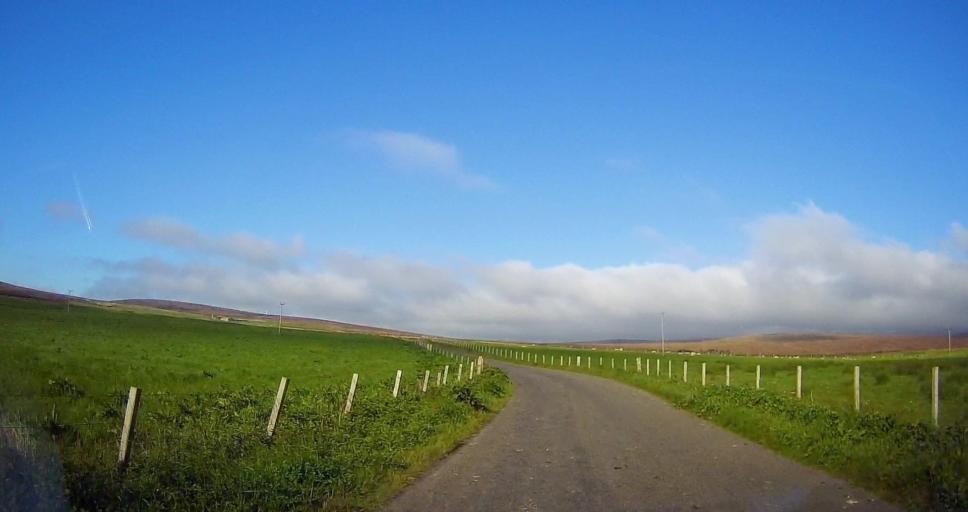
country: GB
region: Scotland
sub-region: Orkney Islands
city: Stromness
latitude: 59.0861
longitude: -3.1864
